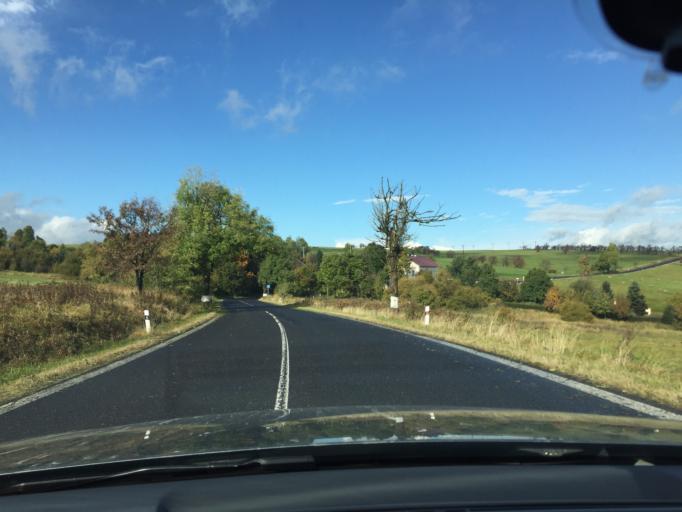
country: CZ
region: Ustecky
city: Chlumec
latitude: 50.7436
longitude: 13.9781
